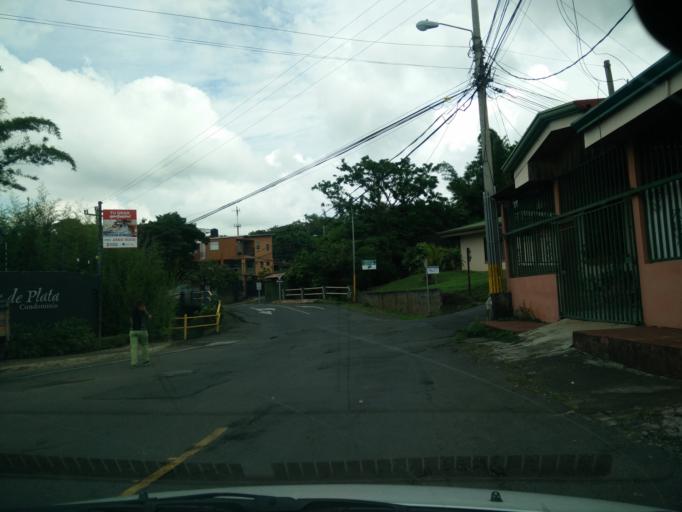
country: CR
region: Heredia
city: San Rafael
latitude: 10.0070
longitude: -84.1036
